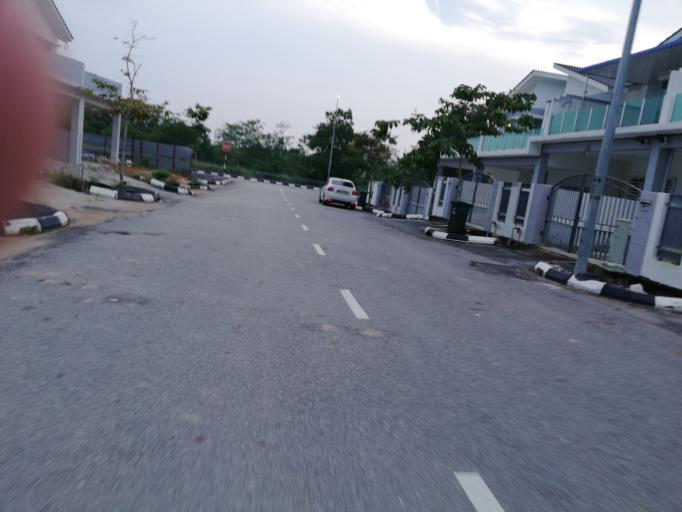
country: MY
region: Kedah
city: Kulim
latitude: 5.3835
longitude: 100.5815
